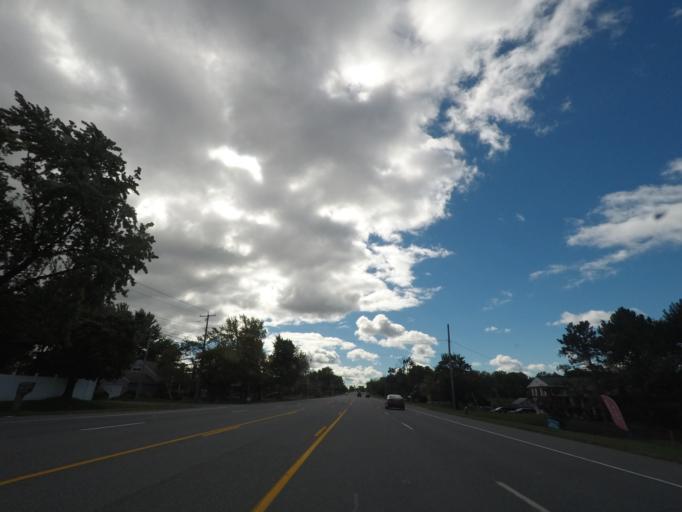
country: US
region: New York
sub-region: Albany County
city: Cohoes
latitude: 42.8006
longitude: -73.7335
